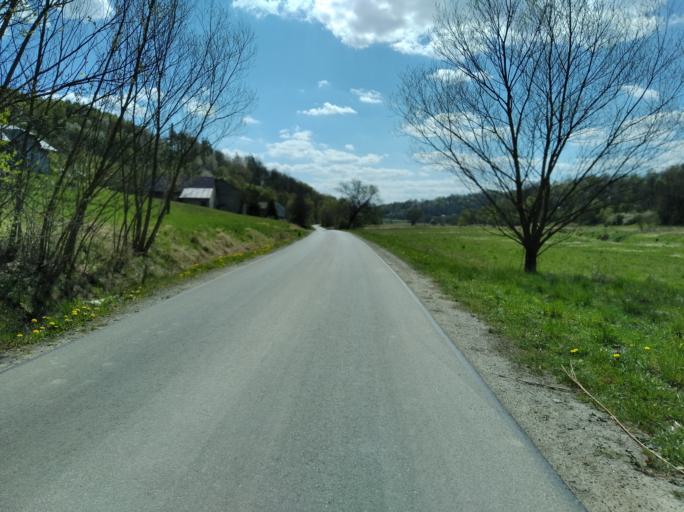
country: PL
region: Subcarpathian Voivodeship
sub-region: Powiat brzozowski
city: Domaradz
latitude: 49.7853
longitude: 21.9536
